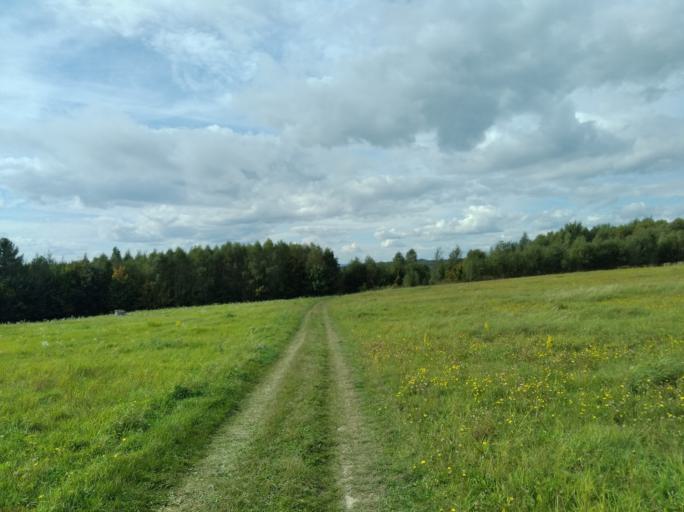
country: PL
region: Subcarpathian Voivodeship
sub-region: Powiat strzyzowski
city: Jawornik
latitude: 49.8342
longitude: 21.9073
